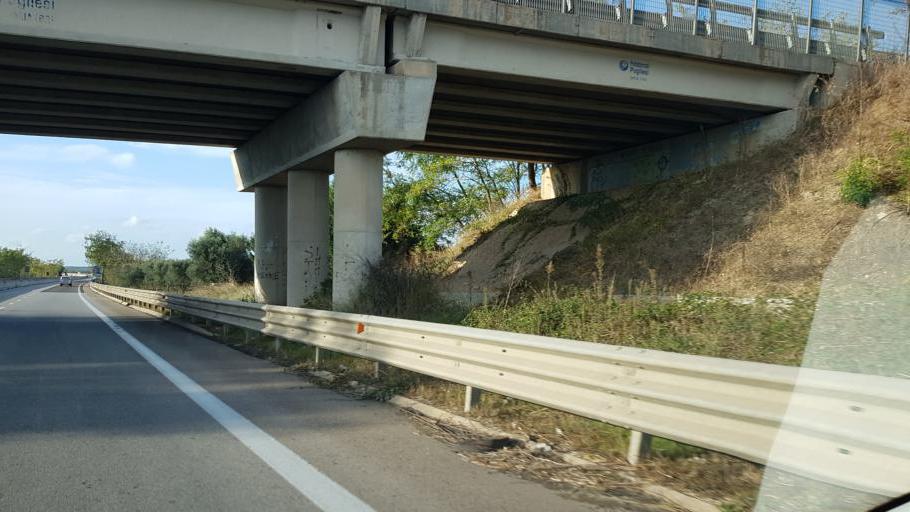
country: IT
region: Apulia
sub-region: Provincia di Brindisi
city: Francavilla Fontana
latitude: 40.5421
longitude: 17.6017
